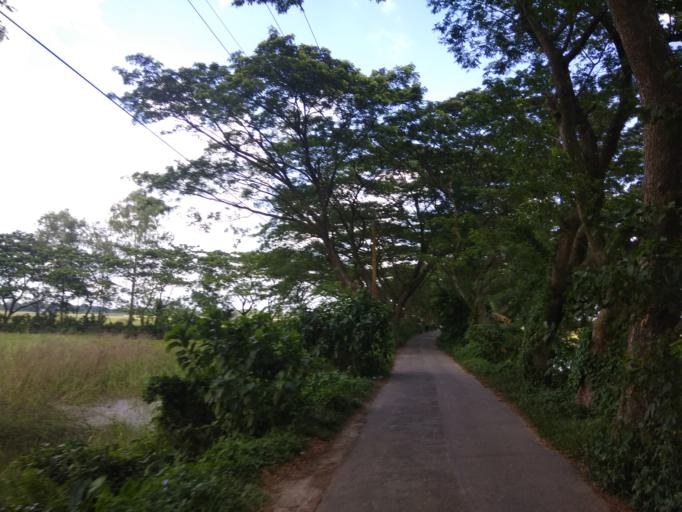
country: BD
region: Dhaka
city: Narayanganj
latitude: 23.4610
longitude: 90.4522
